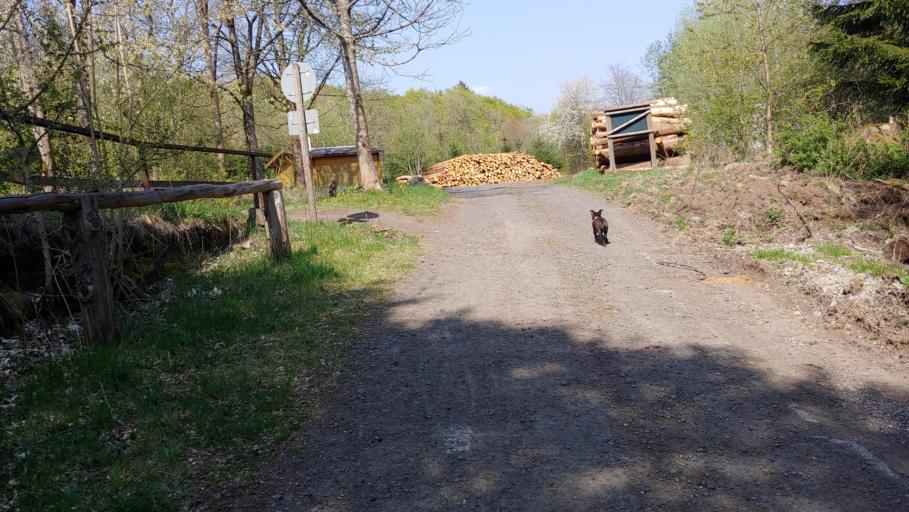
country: DE
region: Hesse
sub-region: Regierungsbezirk Kassel
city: Baunatal
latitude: 51.3111
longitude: 9.3607
